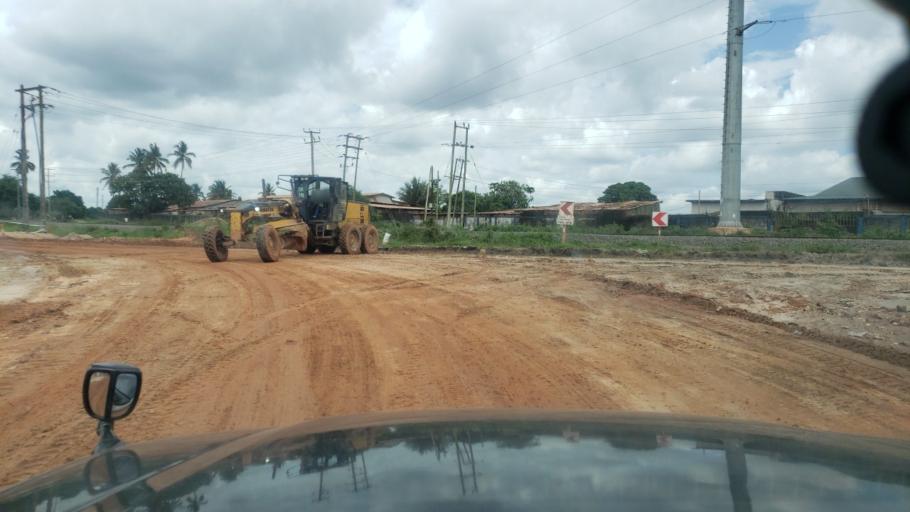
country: TZ
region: Pwani
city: Kisarawe
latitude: -6.8849
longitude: 39.1465
